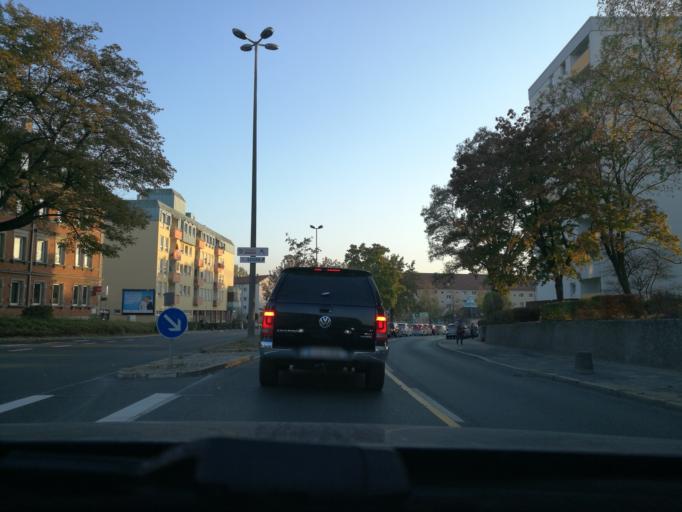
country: DE
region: Bavaria
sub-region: Regierungsbezirk Mittelfranken
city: Furth
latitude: 49.4819
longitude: 10.9983
